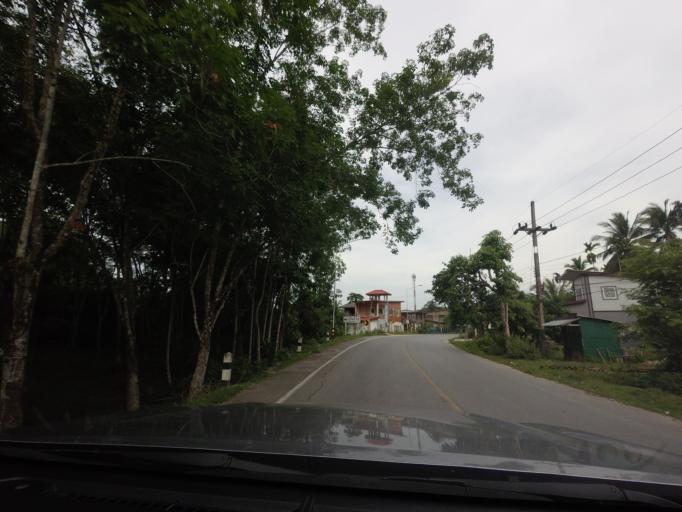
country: TH
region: Yala
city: Raman
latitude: 6.4400
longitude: 101.4545
